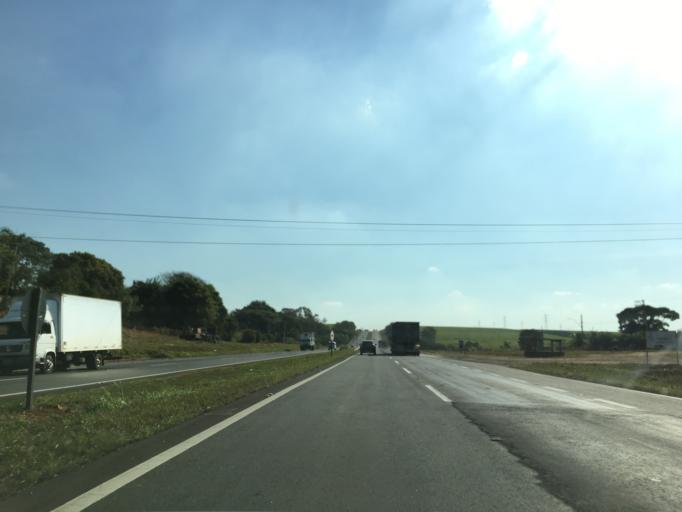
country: BR
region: Sao Paulo
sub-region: Piracicaba
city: Piracicaba
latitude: -22.7266
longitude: -47.5581
